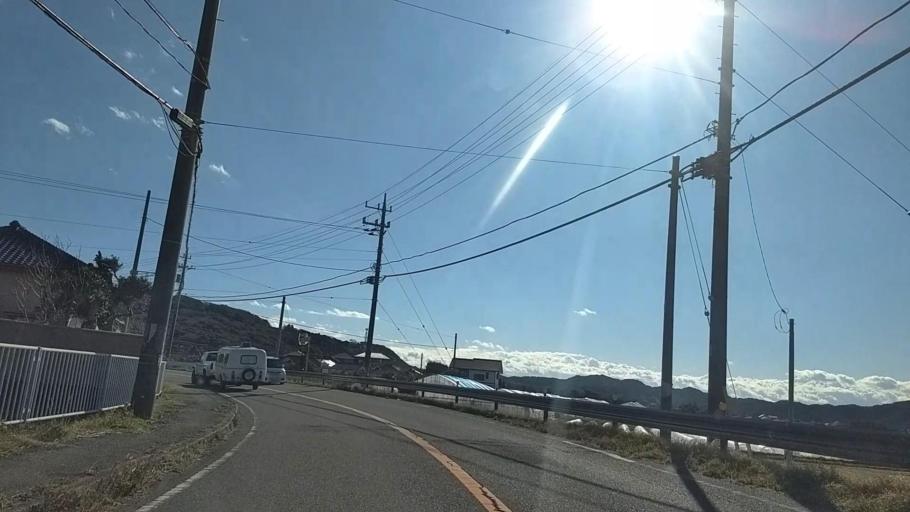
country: JP
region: Chiba
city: Tateyama
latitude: 34.9422
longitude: 139.8377
